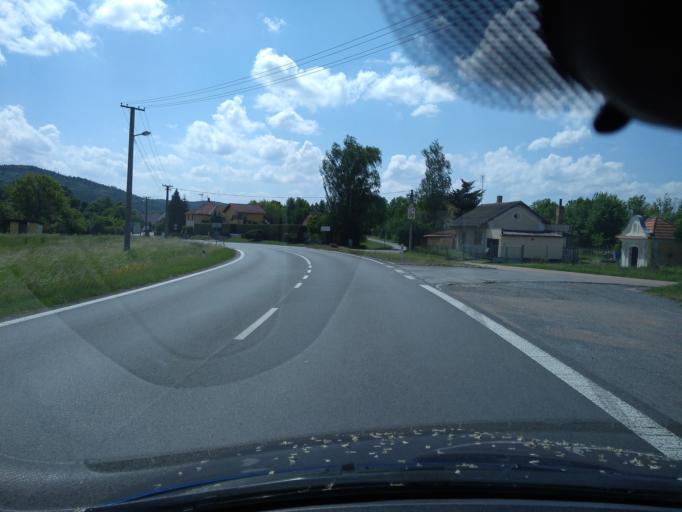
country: CZ
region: Plzensky
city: Prestice
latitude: 49.5504
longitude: 13.3154
